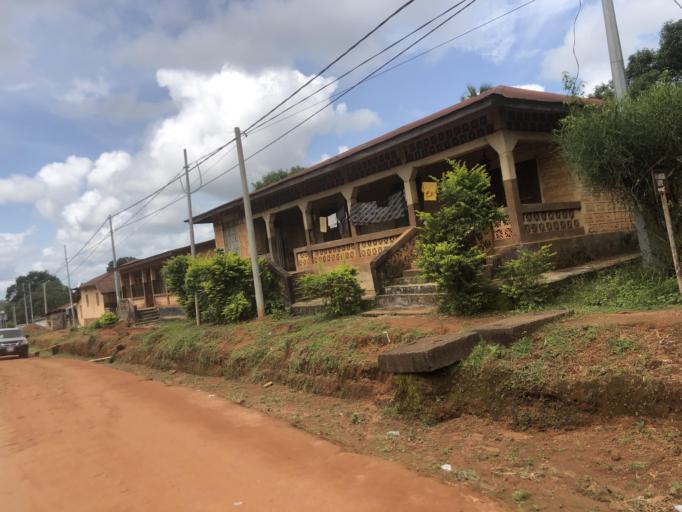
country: SL
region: Northern Province
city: Makeni
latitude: 8.8729
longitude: -12.0520
